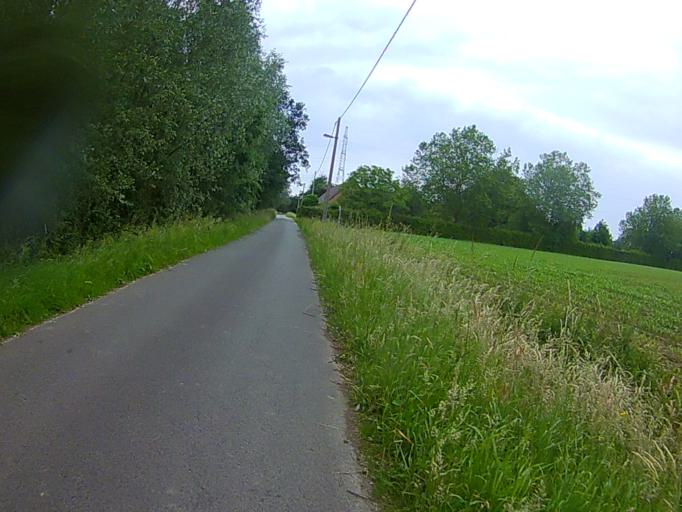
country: BE
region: Flanders
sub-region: Provincie Antwerpen
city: Lier
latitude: 51.1560
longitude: 4.5456
